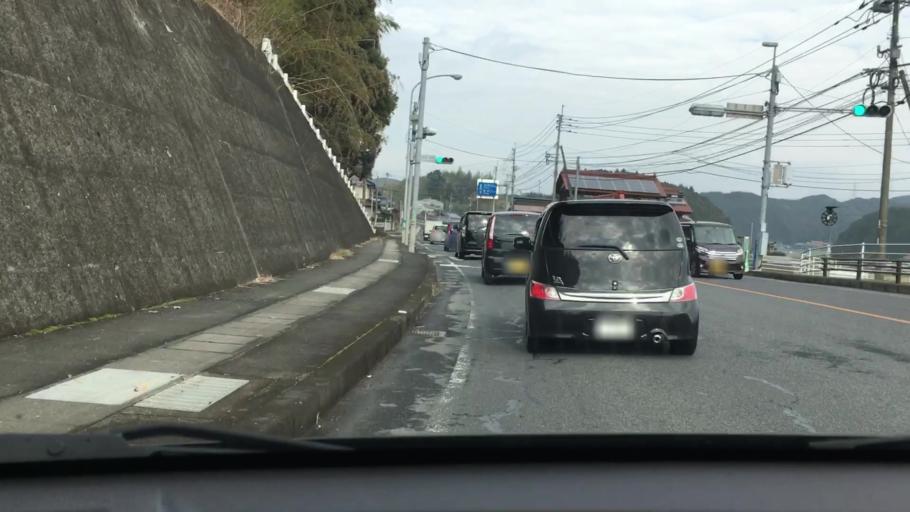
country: JP
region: Saga Prefecture
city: Imaricho-ko
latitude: 33.3064
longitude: 129.9258
